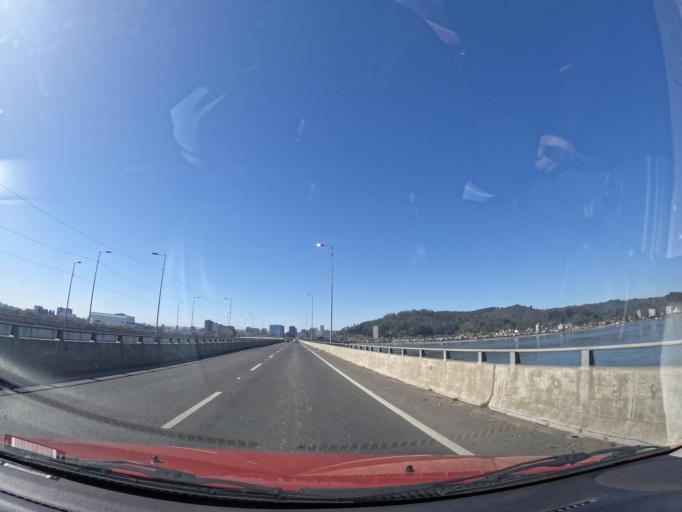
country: CL
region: Biobio
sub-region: Provincia de Concepcion
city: Concepcion
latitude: -36.8397
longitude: -73.0686
